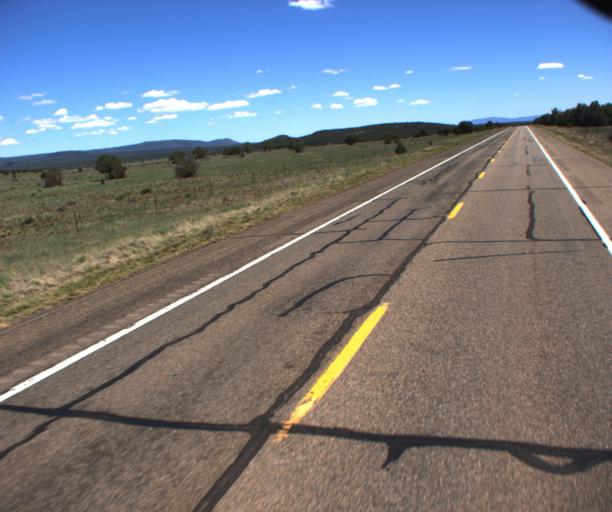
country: US
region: Arizona
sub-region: Yavapai County
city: Paulden
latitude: 35.1543
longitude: -112.4522
